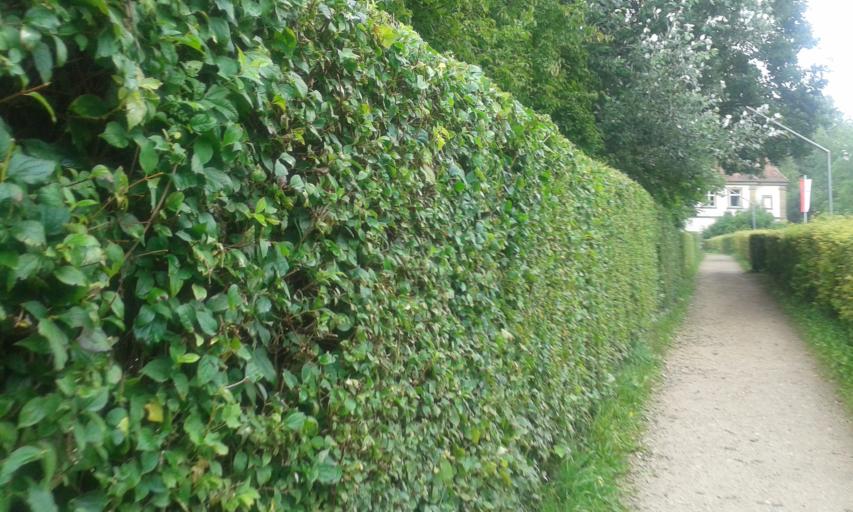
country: DE
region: Bavaria
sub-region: Upper Franconia
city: Bamberg
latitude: 49.8852
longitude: 10.8869
